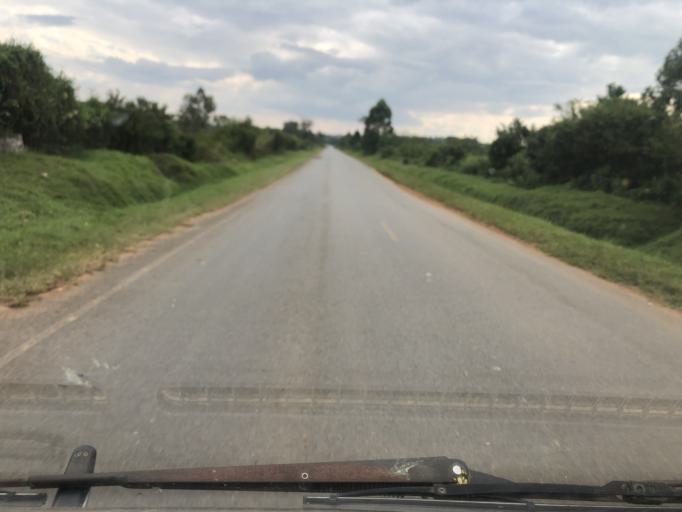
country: UG
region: Western Region
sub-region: Sheema District
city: Kibingo
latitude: -0.5801
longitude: 30.4326
